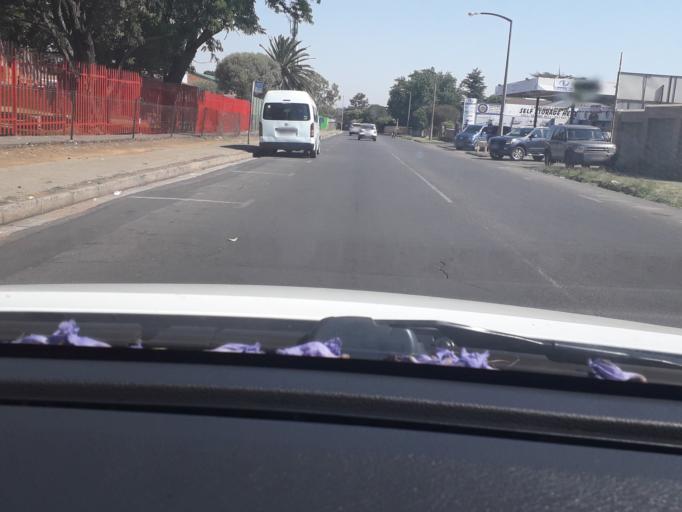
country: ZA
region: Gauteng
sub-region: Ekurhuleni Metropolitan Municipality
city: Benoni
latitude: -26.1875
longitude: 28.3027
